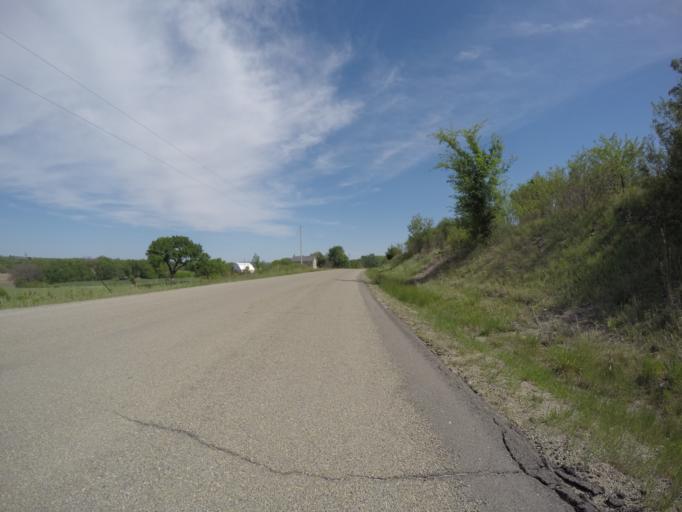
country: US
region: Kansas
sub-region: Riley County
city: Ogden
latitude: 39.0462
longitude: -96.6381
